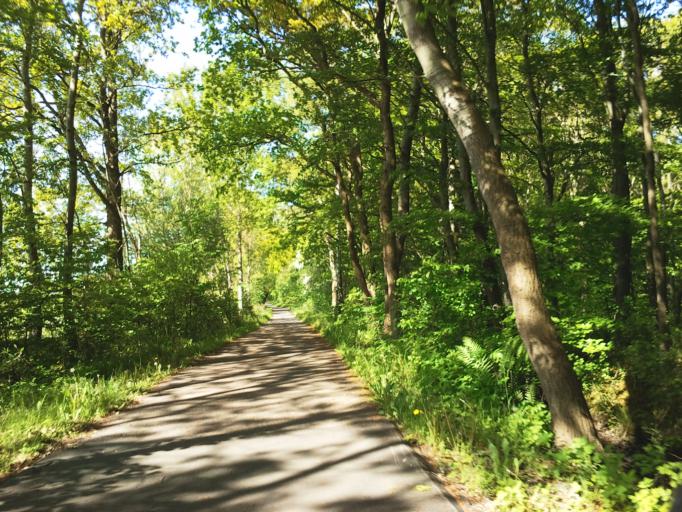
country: DE
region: Mecklenburg-Vorpommern
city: Nienhagen
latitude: 54.1353
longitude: 12.1841
